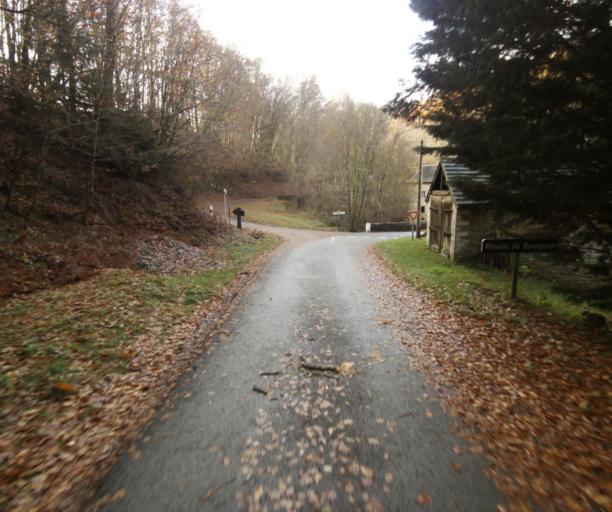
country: FR
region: Limousin
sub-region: Departement de la Correze
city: Sainte-Fereole
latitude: 45.2114
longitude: 1.6312
